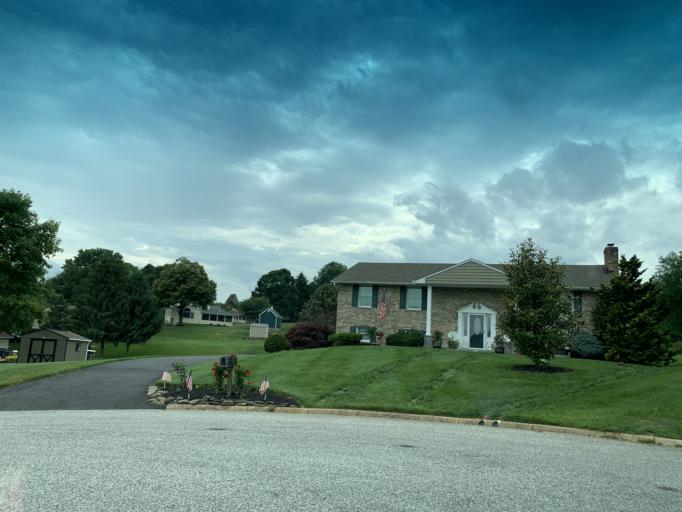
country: US
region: Maryland
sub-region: Harford County
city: Fallston
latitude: 39.5345
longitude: -76.4331
